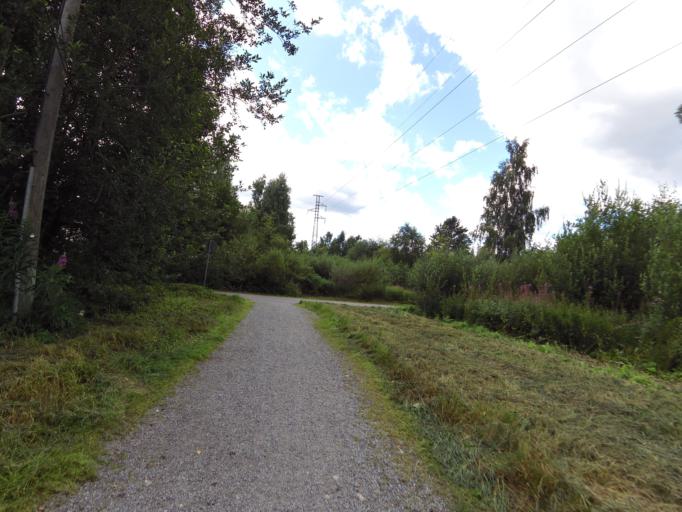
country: FI
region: Pirkanmaa
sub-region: Tampere
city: Yloejaervi
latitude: 61.5118
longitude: 23.6039
